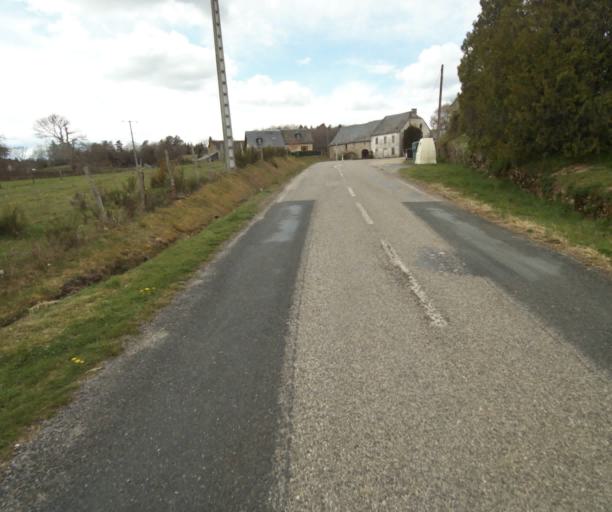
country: FR
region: Limousin
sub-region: Departement de la Correze
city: Argentat
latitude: 45.2115
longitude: 1.9206
